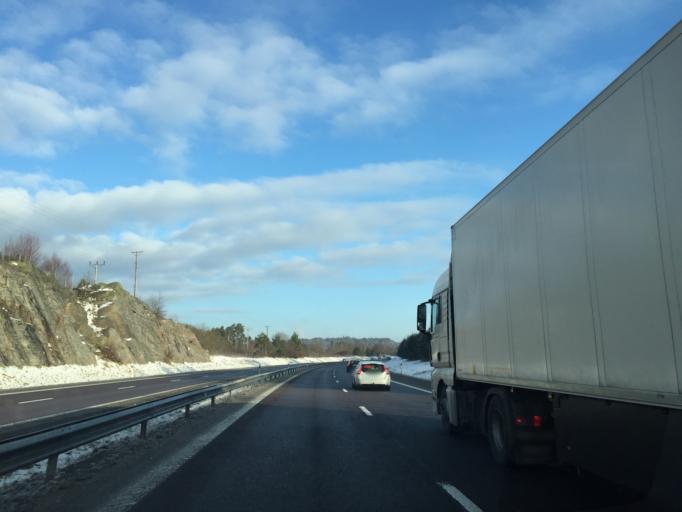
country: SE
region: Vaestra Goetaland
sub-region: Stenungsunds Kommun
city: Stora Hoga
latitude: 58.0372
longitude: 11.8457
